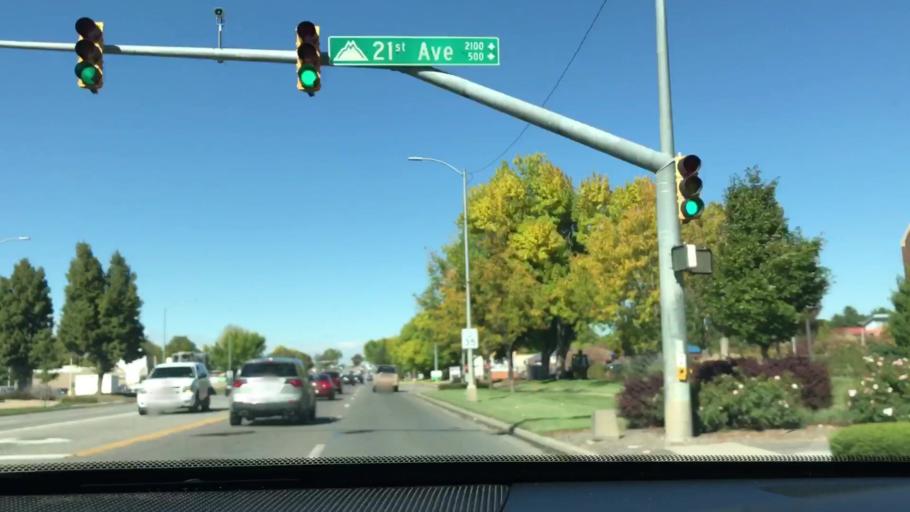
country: US
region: Colorado
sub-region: Boulder County
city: Longmont
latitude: 40.1959
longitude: -105.1023
